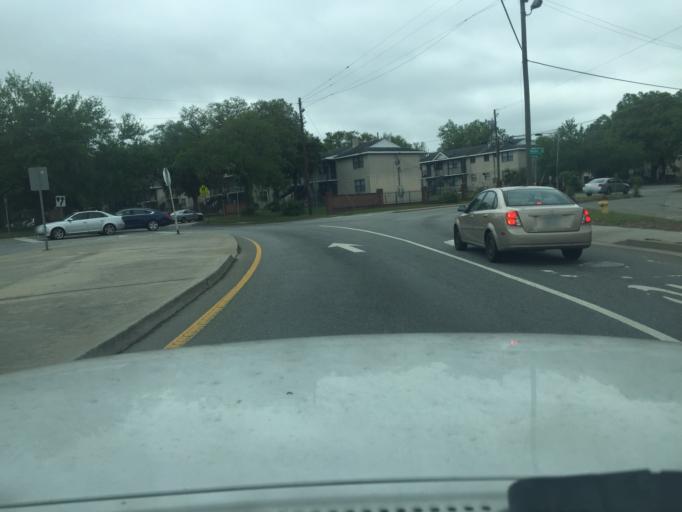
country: US
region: Georgia
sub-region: Chatham County
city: Savannah
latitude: 32.0720
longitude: -81.0837
